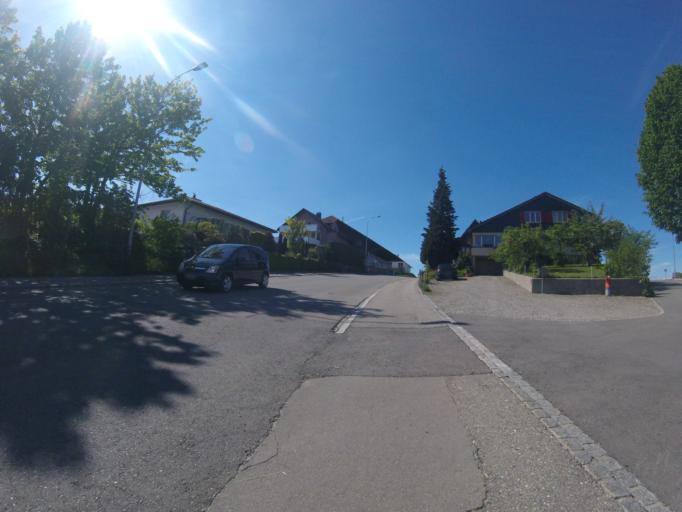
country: CH
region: Saint Gallen
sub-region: Wahlkreis Toggenburg
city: Kirchberg
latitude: 47.4193
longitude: 9.0628
